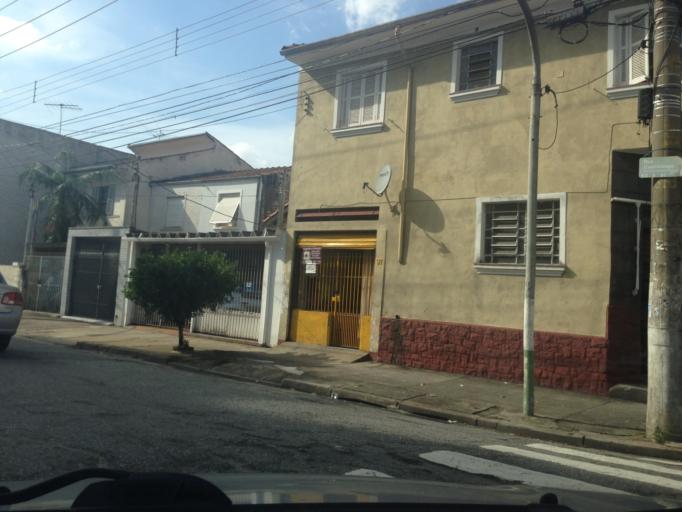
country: BR
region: Sao Paulo
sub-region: Sao Paulo
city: Sao Paulo
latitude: -23.5213
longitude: -46.7106
